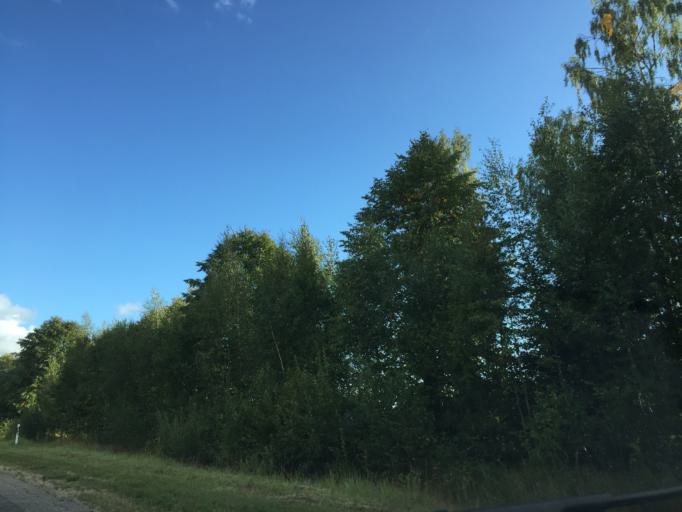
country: LV
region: Krimulda
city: Ragana
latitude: 57.2355
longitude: 24.6757
